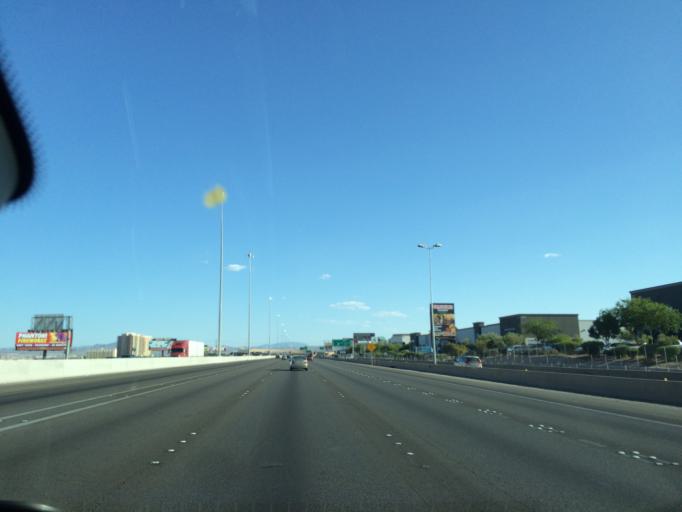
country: US
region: Nevada
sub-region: Clark County
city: Paradise
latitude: 36.0548
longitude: -115.1809
